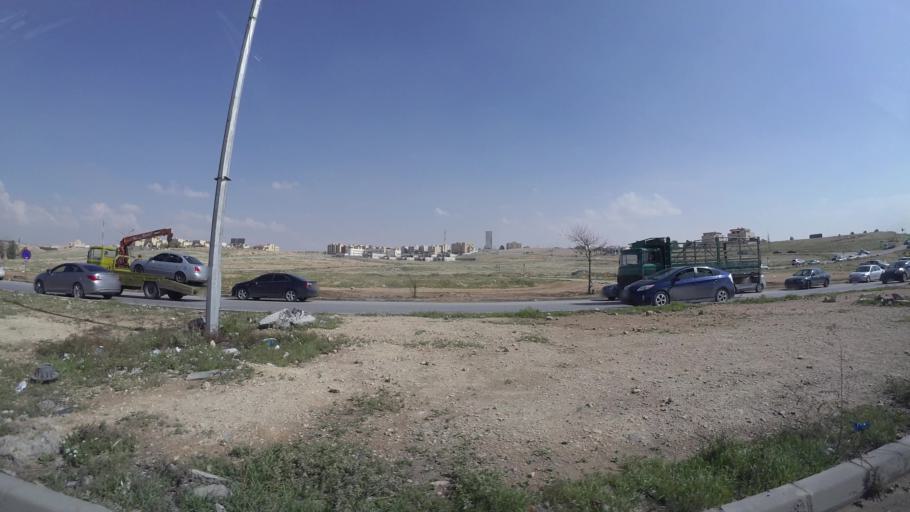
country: JO
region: Zarqa
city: Zarqa
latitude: 32.0770
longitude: 36.1042
